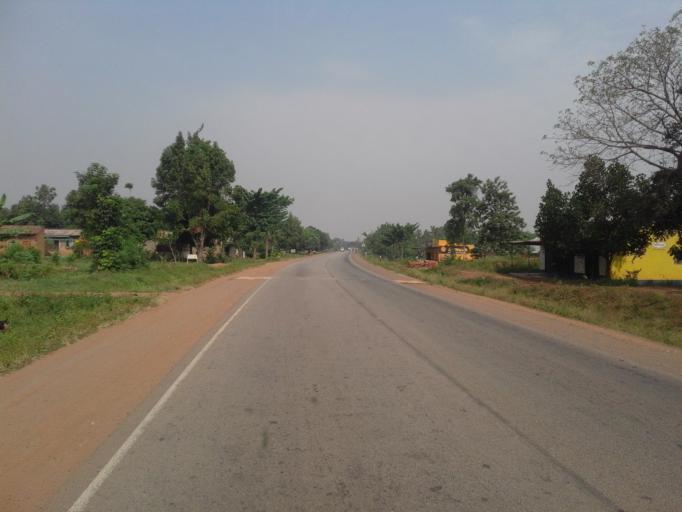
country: UG
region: Eastern Region
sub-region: Bugiri District
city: Bugiri
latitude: 0.5765
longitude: 33.7413
